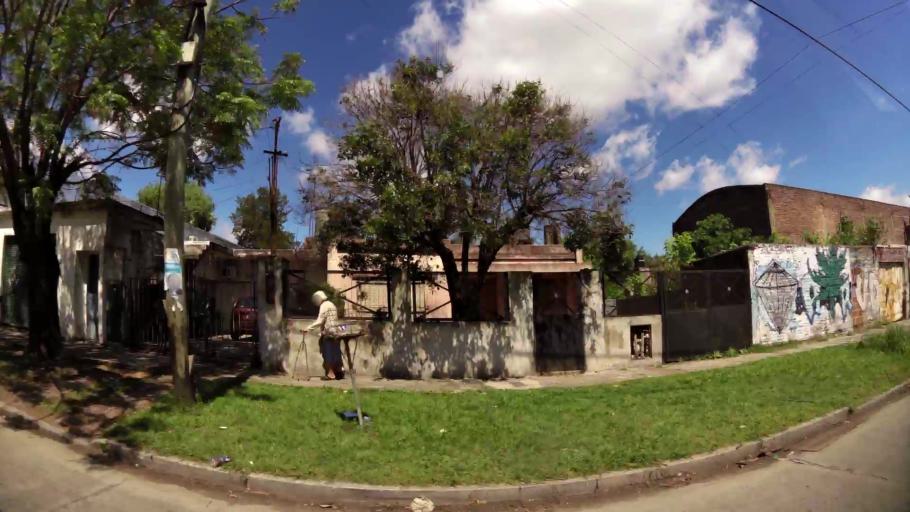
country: AR
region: Buenos Aires F.D.
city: Villa Lugano
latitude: -34.6843
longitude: -58.4344
